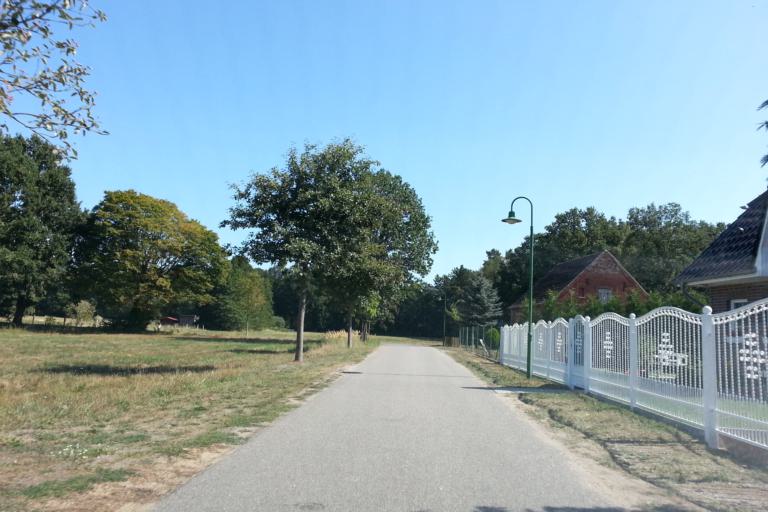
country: DE
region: Mecklenburg-Vorpommern
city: Ferdinandshof
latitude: 53.6404
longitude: 13.9310
